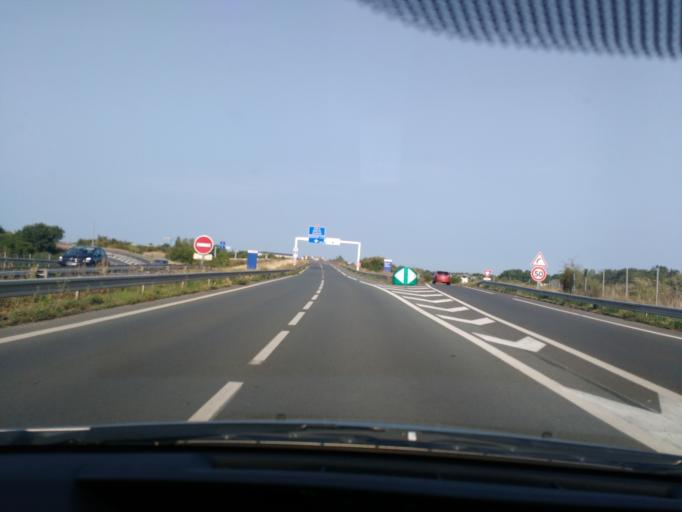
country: FR
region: Pays de la Loire
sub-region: Departement de Maine-et-Loire
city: Angers
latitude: 47.4659
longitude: -0.5188
